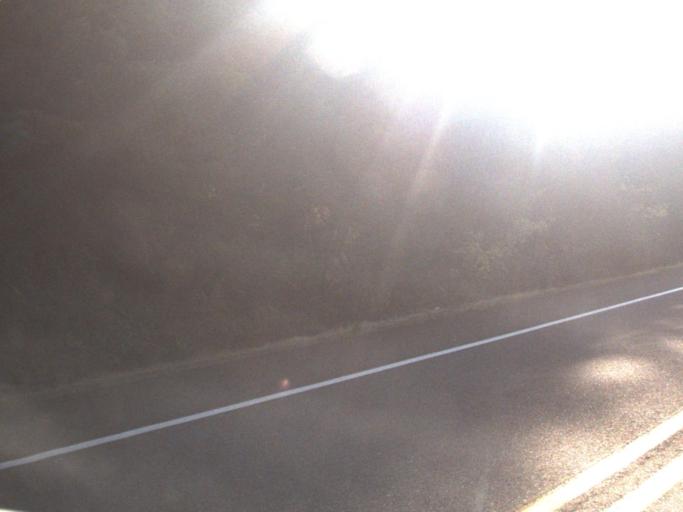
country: US
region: Washington
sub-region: Snohomish County
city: Darrington
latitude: 48.7051
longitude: -120.9459
